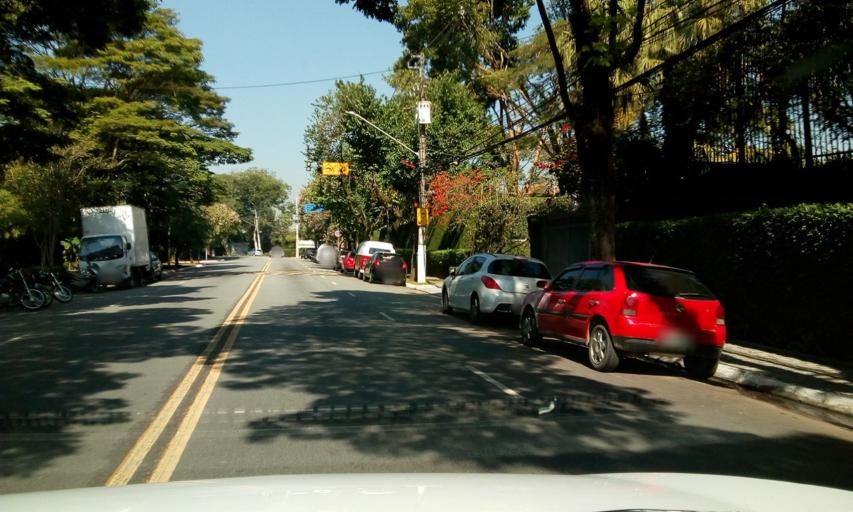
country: BR
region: Sao Paulo
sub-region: Sao Paulo
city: Sao Paulo
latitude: -23.5886
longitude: -46.7060
